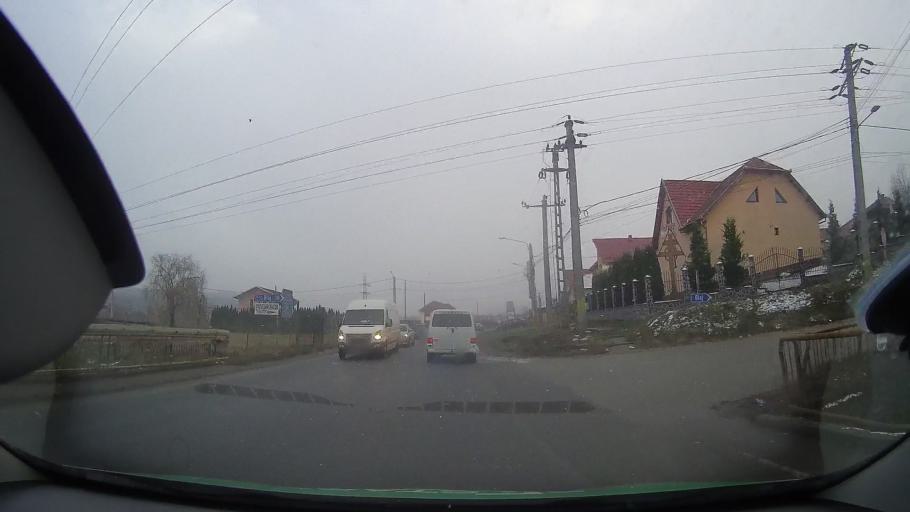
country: RO
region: Mures
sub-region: Municipiul Tarnaveni
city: Tarnaveni
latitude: 46.3150
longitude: 24.2973
